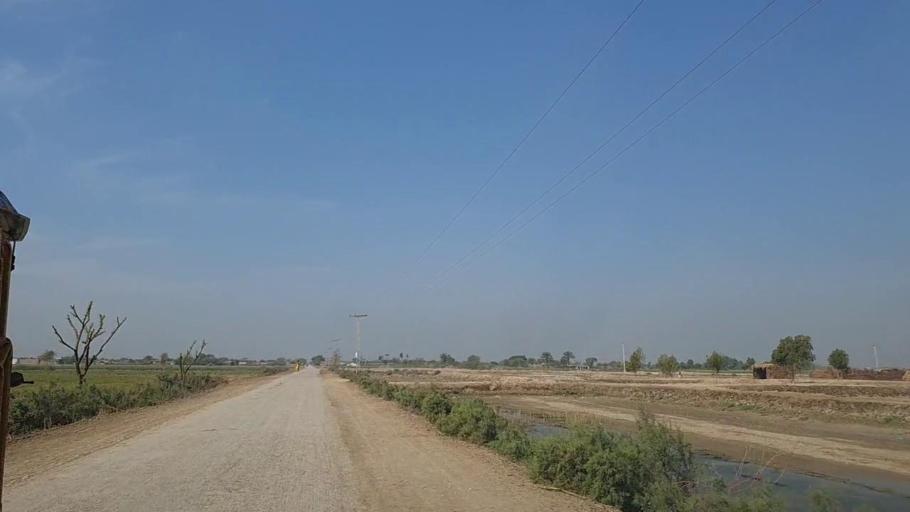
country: PK
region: Sindh
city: Mirpur Khas
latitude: 25.4825
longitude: 68.9938
